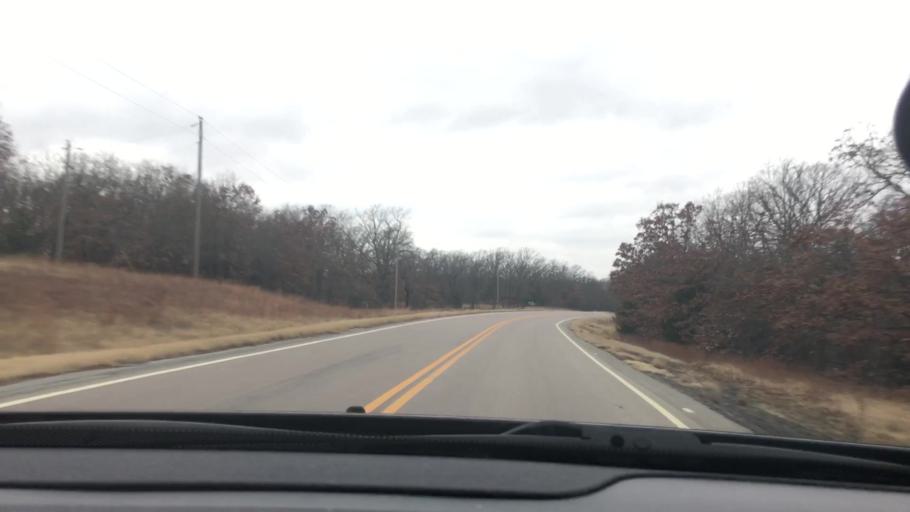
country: US
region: Oklahoma
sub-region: Coal County
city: Coalgate
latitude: 34.3709
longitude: -96.3771
